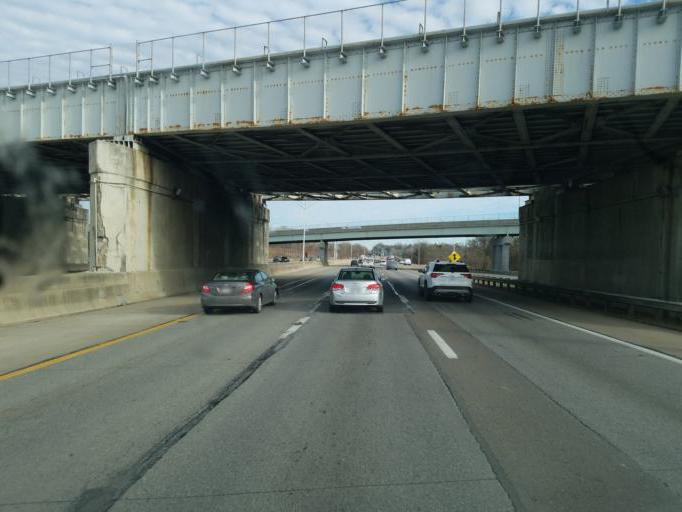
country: US
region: Ohio
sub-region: Franklin County
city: Bexley
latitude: 39.9807
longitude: -82.9528
